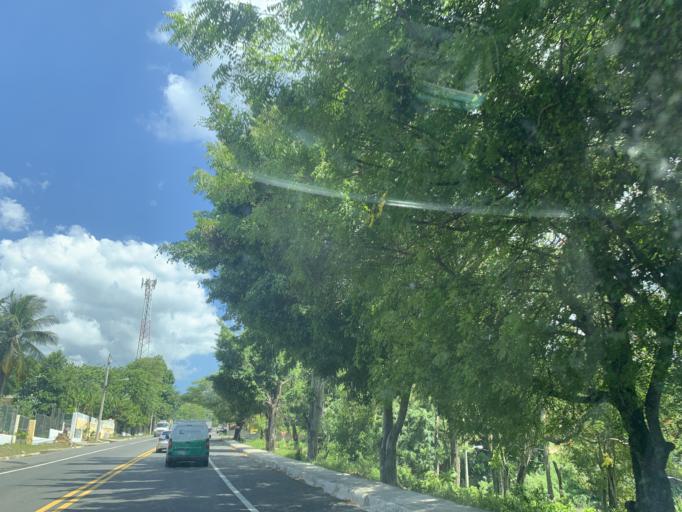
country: DO
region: Puerto Plata
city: Altamira
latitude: 19.6790
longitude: -70.8365
